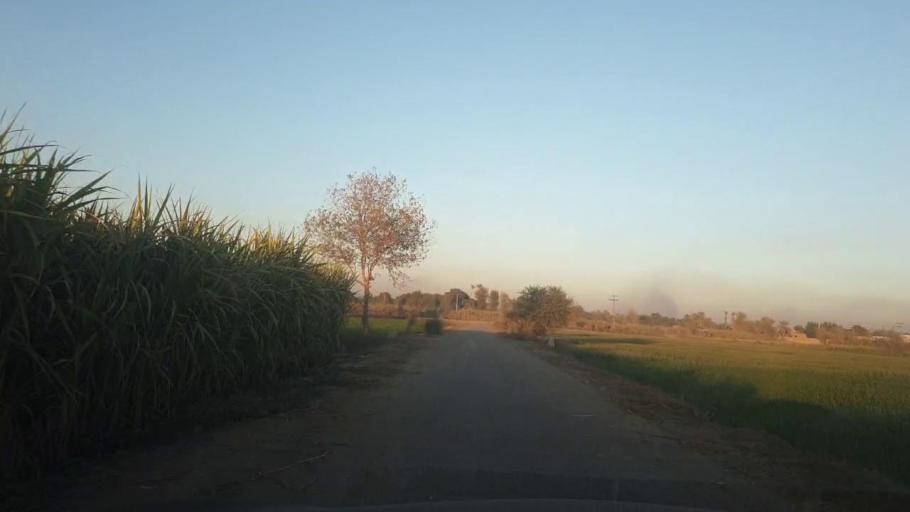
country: PK
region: Sindh
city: Ghotki
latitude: 28.0276
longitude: 69.2915
